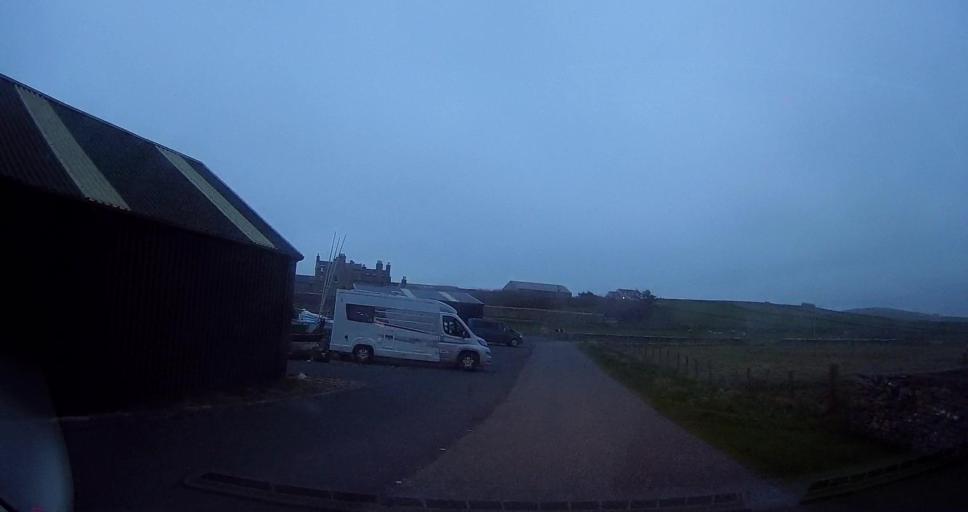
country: GB
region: Scotland
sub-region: Shetland Islands
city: Sandwick
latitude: 60.0066
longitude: -1.2219
